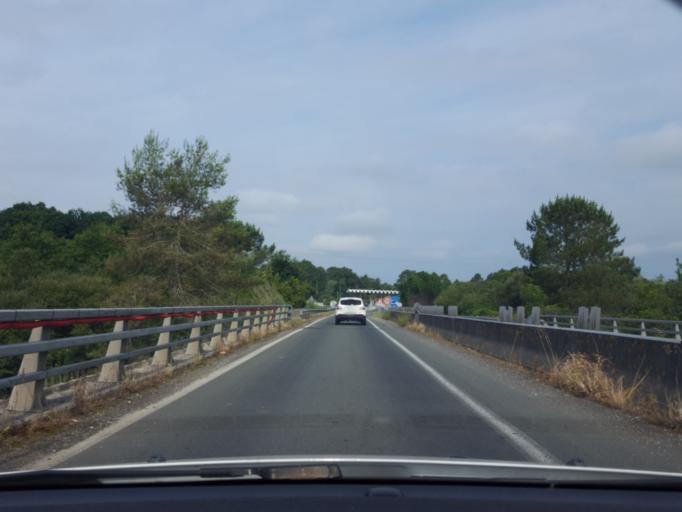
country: FR
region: Aquitaine
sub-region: Departement des Landes
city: Ondres
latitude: 43.5410
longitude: -1.4314
